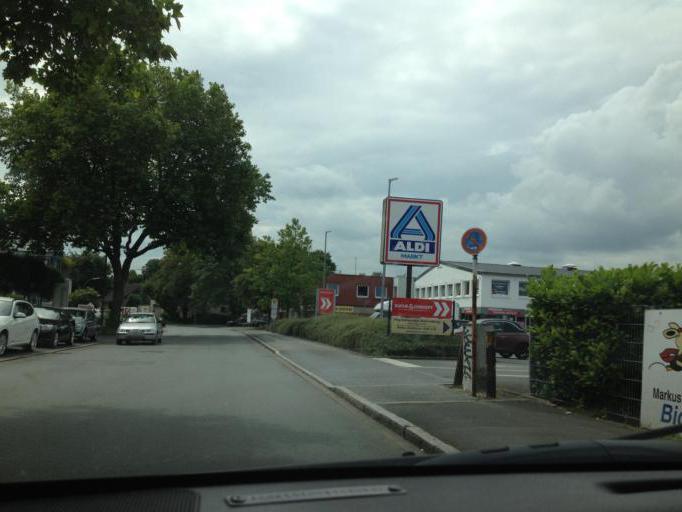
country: DE
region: North Rhine-Westphalia
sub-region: Regierungsbezirk Arnsberg
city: Dortmund
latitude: 51.4698
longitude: 7.4322
